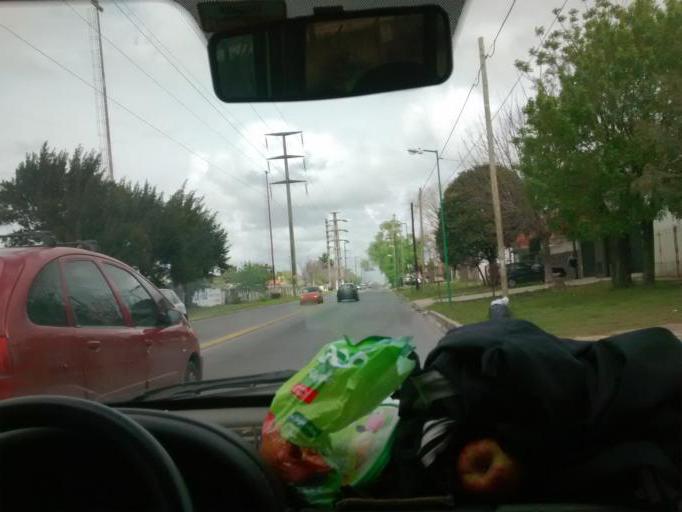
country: AR
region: Buenos Aires
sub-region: Partido de La Plata
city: La Plata
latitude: -34.9456
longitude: -57.9813
